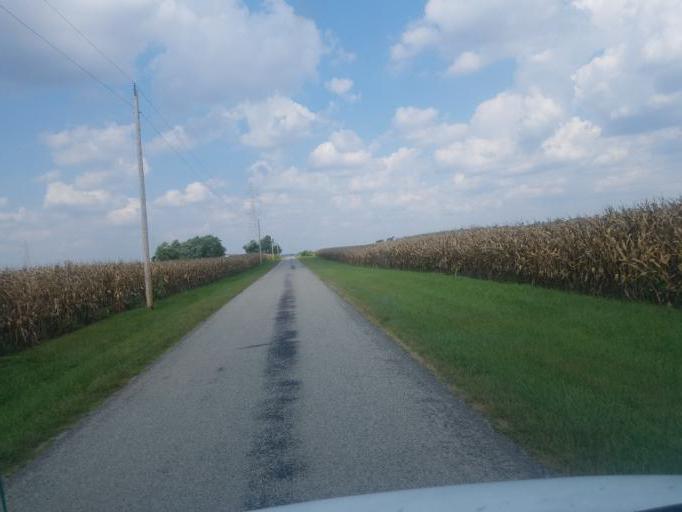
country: US
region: Ohio
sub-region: Hardin County
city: Ada
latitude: 40.6253
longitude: -83.7878
